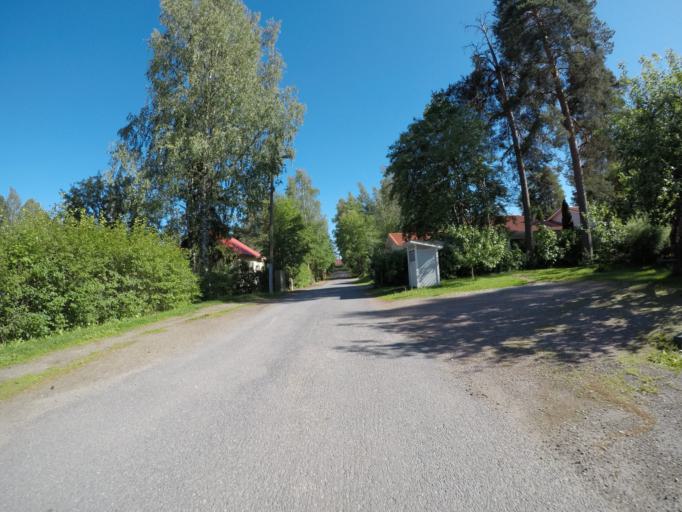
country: FI
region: Haeme
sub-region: Haemeenlinna
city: Haemeenlinna
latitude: 61.0116
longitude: 24.4811
